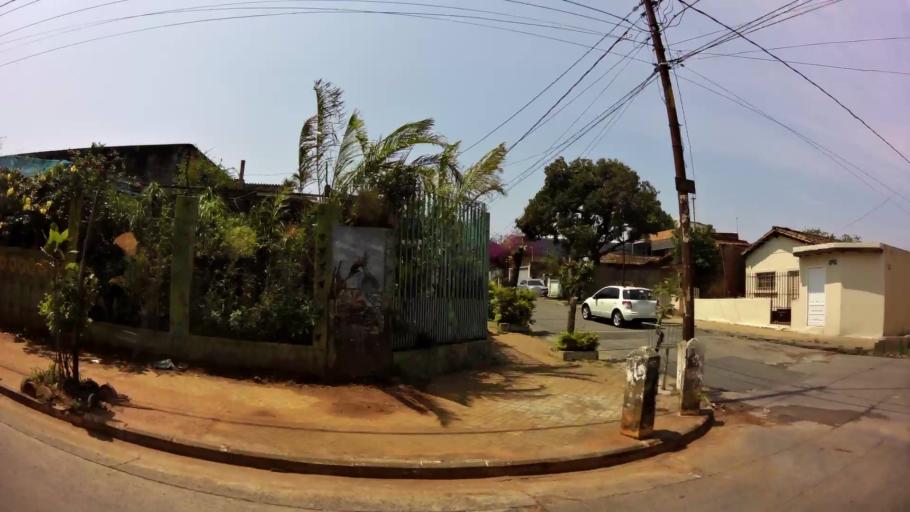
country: PY
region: Asuncion
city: Asuncion
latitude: -25.2979
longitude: -57.6529
